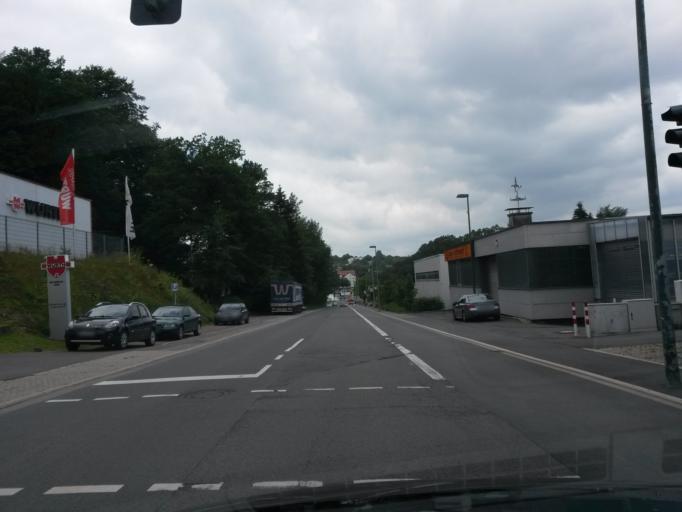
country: DE
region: North Rhine-Westphalia
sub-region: Regierungsbezirk Arnsberg
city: Luedenscheid
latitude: 51.2143
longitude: 7.6576
